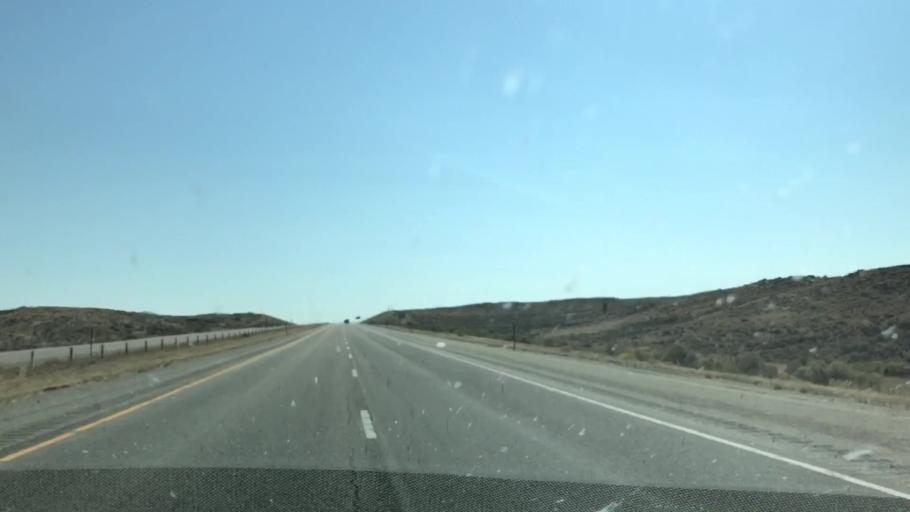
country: US
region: Wyoming
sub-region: Sweetwater County
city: Rock Springs
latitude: 41.6466
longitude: -108.5934
